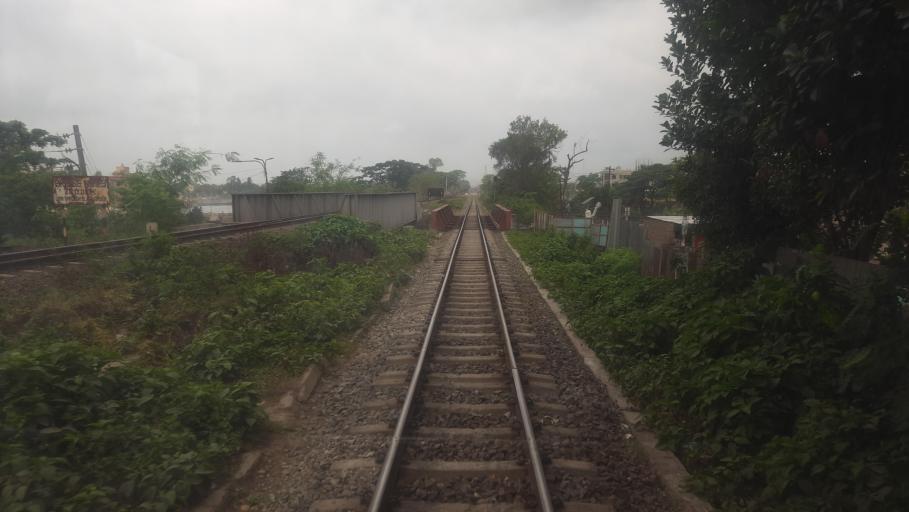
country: BD
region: Dhaka
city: Bhairab Bazar
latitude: 24.0505
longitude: 90.9854
